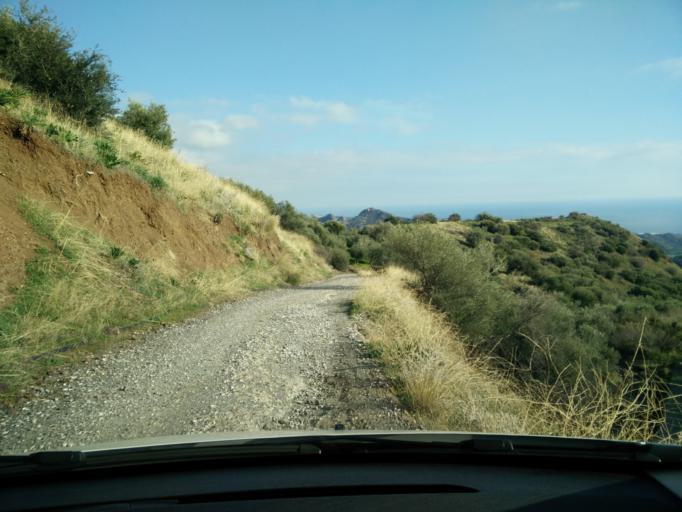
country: GR
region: Crete
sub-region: Nomos Lasithiou
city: Gra Liyia
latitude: 35.0321
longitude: 25.5681
